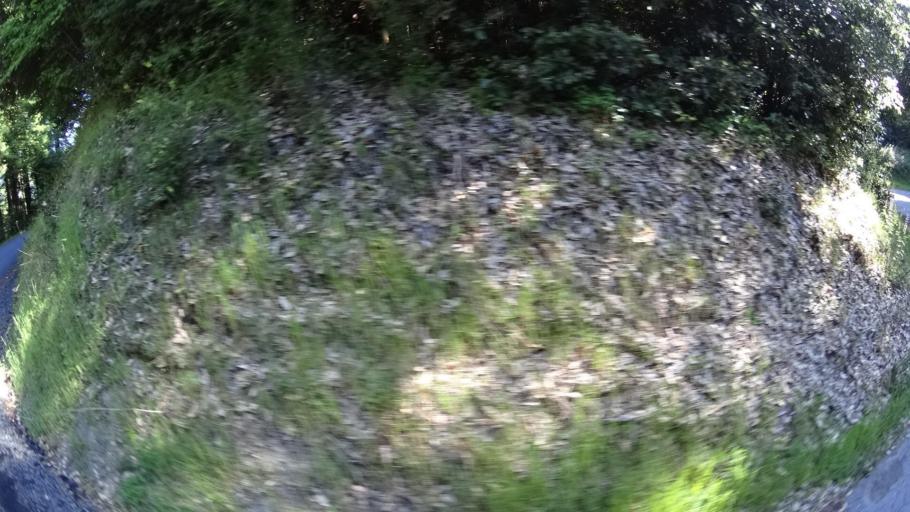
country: US
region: California
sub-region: Humboldt County
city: Rio Dell
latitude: 40.4453
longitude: -123.9762
